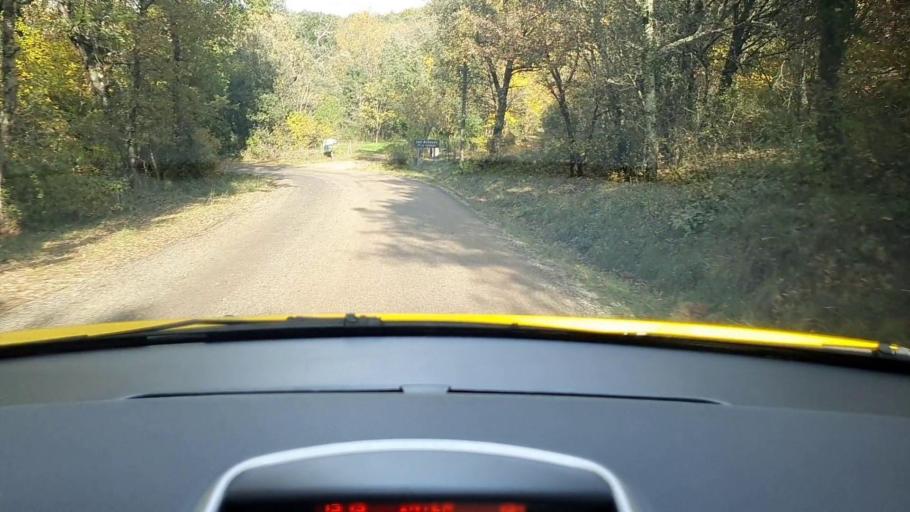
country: FR
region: Languedoc-Roussillon
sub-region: Departement du Gard
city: Anduze
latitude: 44.0505
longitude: 3.9242
